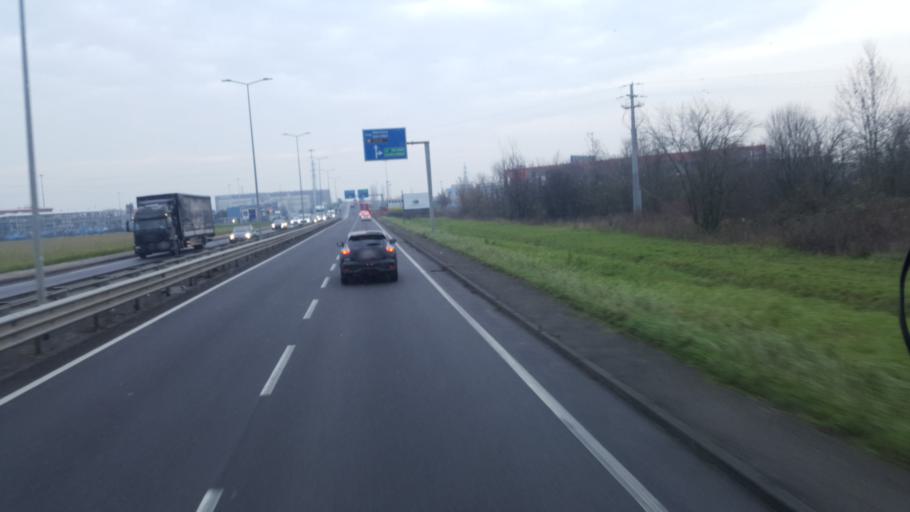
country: IT
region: Emilia-Romagna
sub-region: Provincia di Parma
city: Baganzola
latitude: 44.8341
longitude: 10.3337
